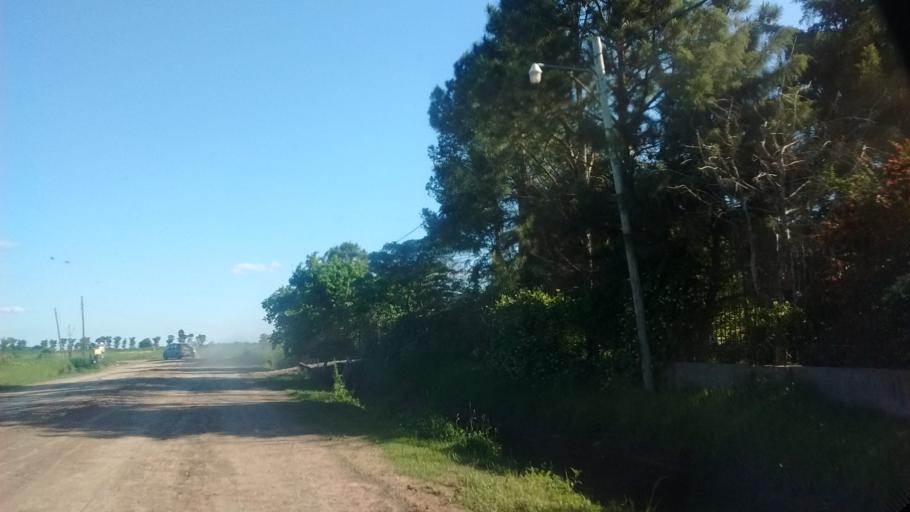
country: AR
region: Santa Fe
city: Funes
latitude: -32.8633
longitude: -60.8031
